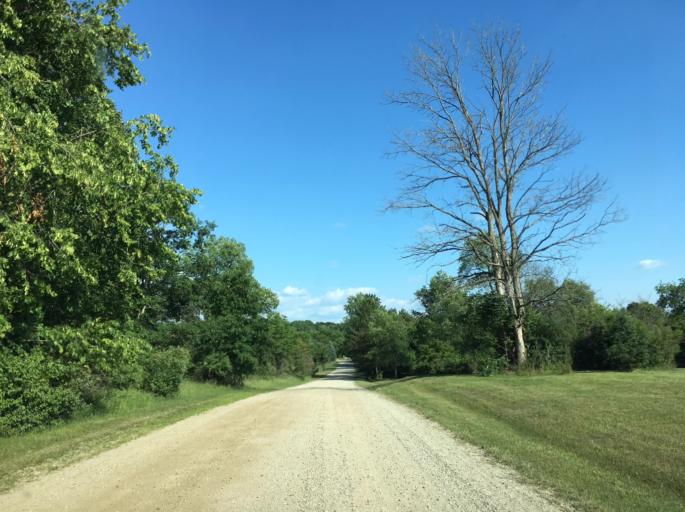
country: US
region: Michigan
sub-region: Osceola County
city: Evart
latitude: 43.8632
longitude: -85.3750
